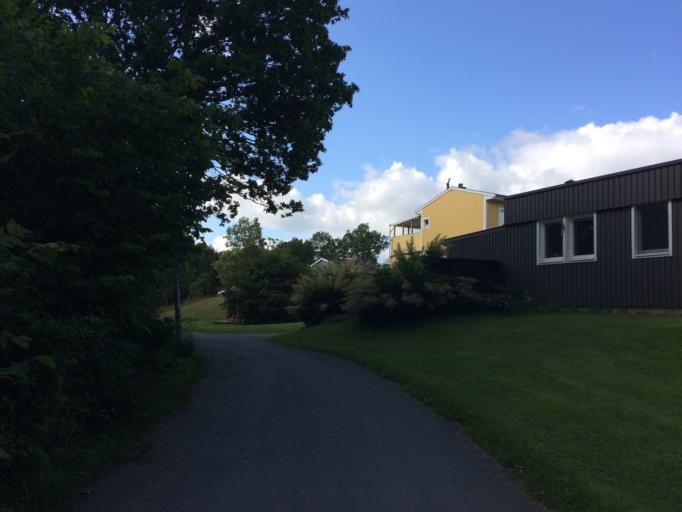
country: SE
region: Stockholm
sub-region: Sollentuna Kommun
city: Sollentuna
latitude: 59.4603
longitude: 17.9039
